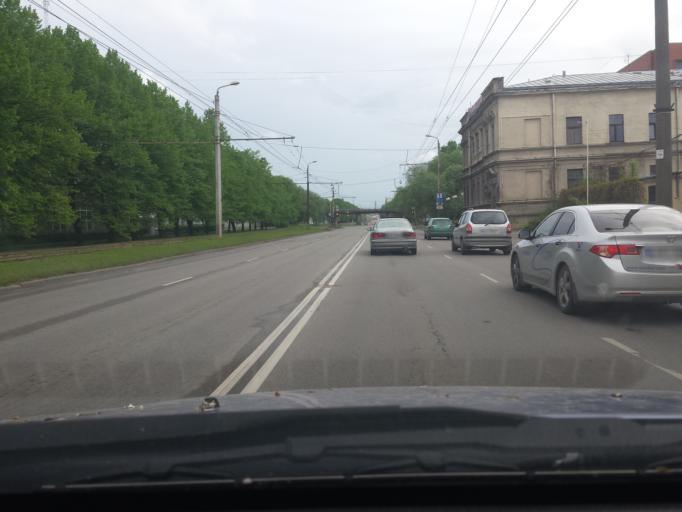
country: LV
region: Riga
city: Riga
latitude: 56.9788
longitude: 24.1152
